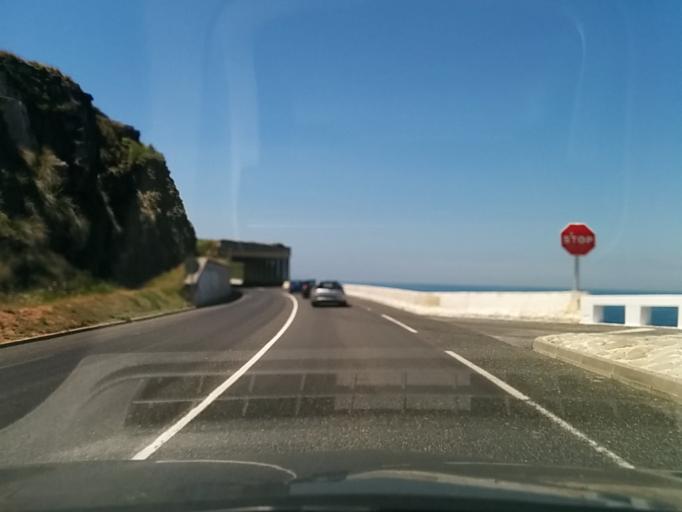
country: ES
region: Basque Country
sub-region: Provincia de Guipuzcoa
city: Getaria
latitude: 43.3085
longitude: -2.2163
